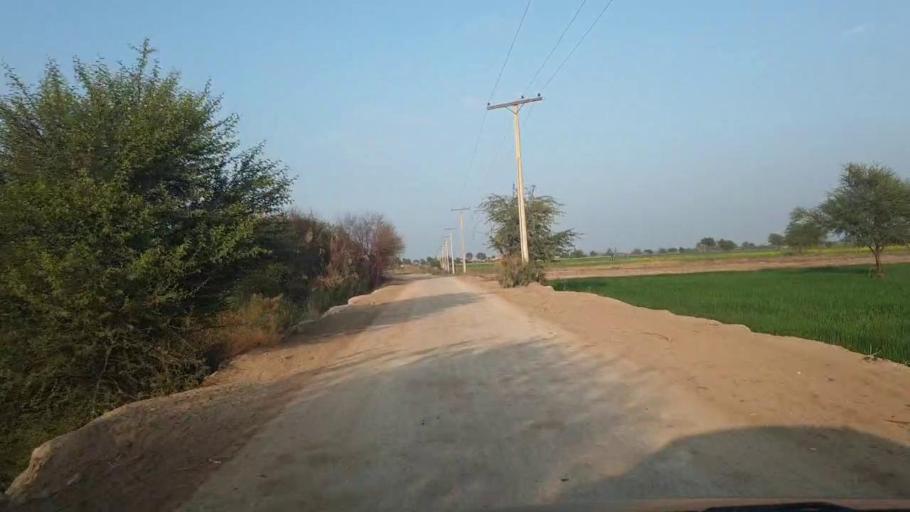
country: PK
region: Sindh
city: Berani
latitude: 25.8607
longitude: 68.7385
